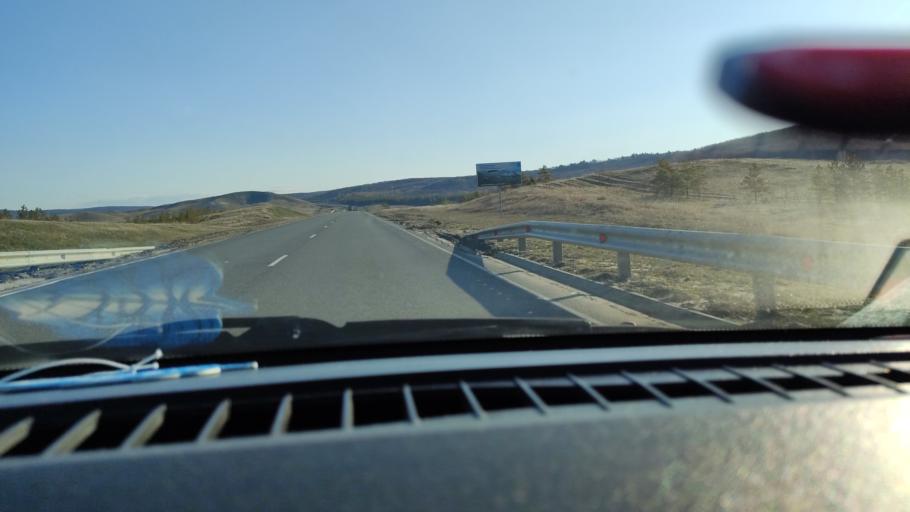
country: RU
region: Saratov
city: Alekseyevka
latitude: 52.3596
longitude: 47.9523
